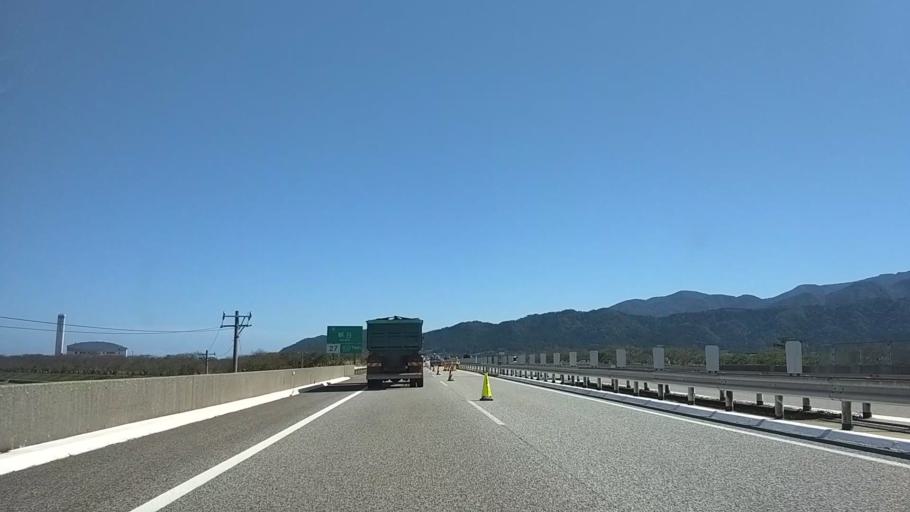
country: JP
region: Toyama
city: Nyuzen
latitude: 36.9333
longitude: 137.5373
